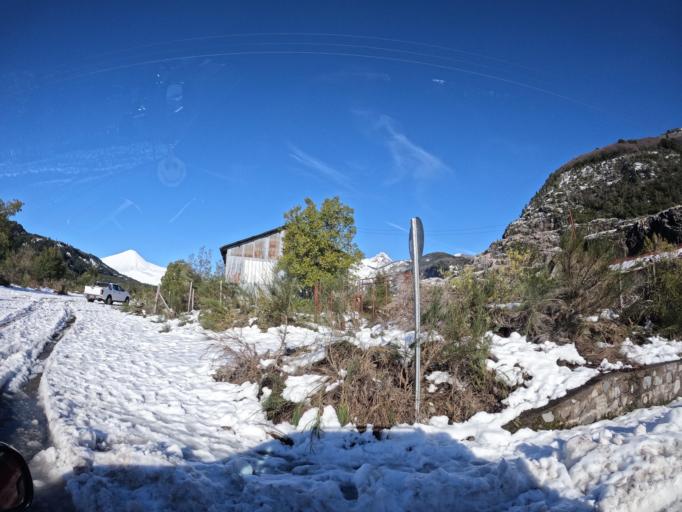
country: CL
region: Biobio
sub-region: Provincia de Nuble
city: Coihueco
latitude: -37.3717
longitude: -71.4934
